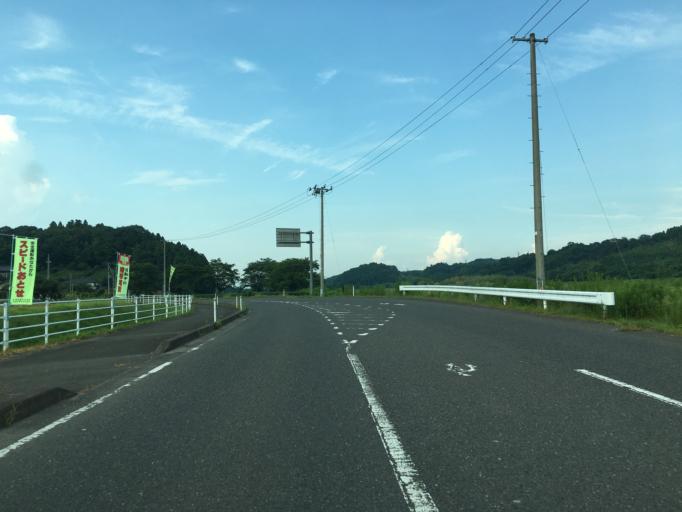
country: JP
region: Fukushima
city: Nihommatsu
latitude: 37.5552
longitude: 140.4337
